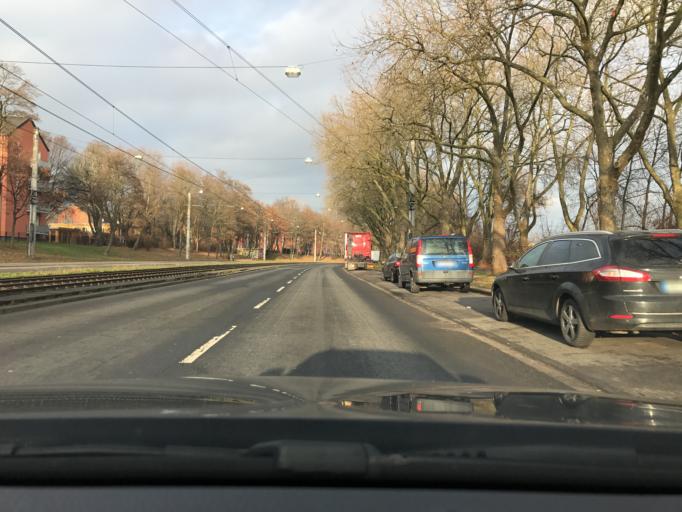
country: DE
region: North Rhine-Westphalia
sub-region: Regierungsbezirk Koln
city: Buchforst
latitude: 50.9507
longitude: 6.9955
